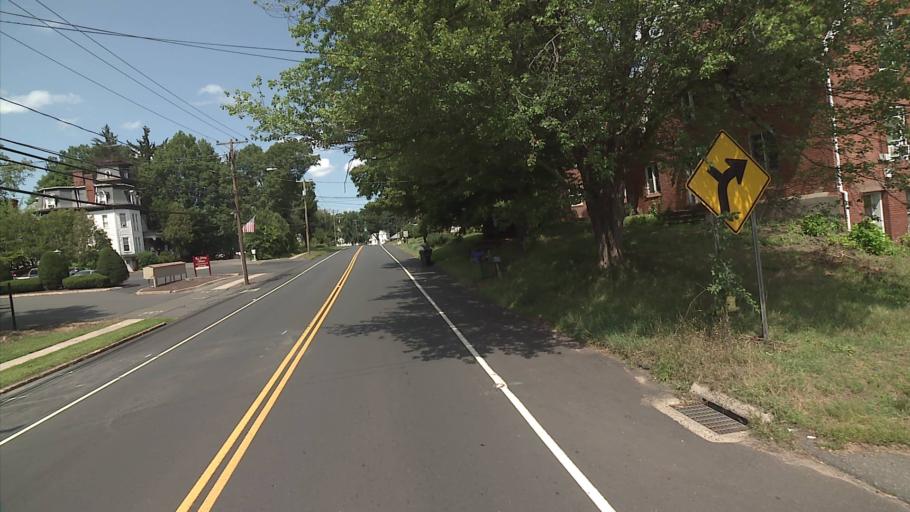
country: US
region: Connecticut
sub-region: Hartford County
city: Broad Brook
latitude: 41.9180
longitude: -72.5460
